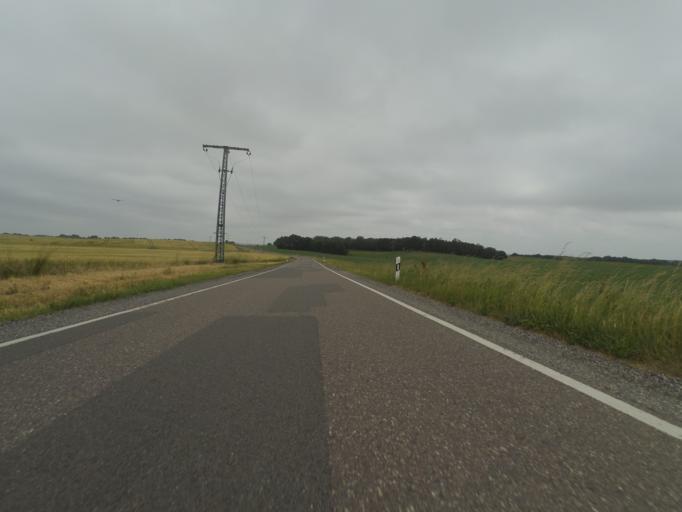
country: DE
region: Mecklenburg-Vorpommern
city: Gaegelow
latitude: 53.6937
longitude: 11.8916
